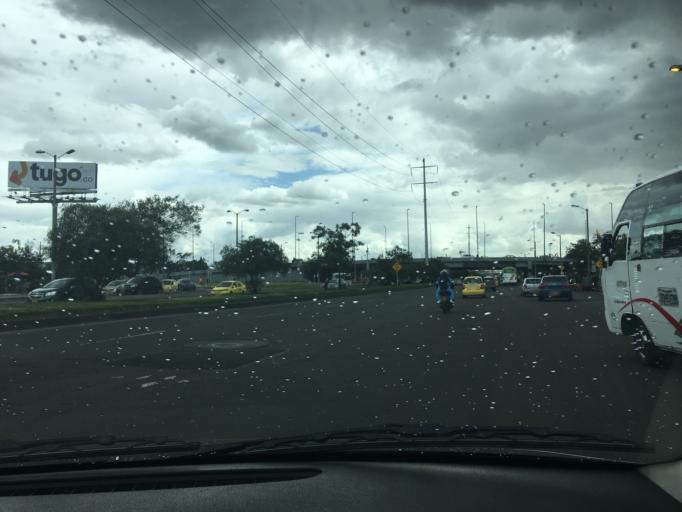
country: CO
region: Bogota D.C.
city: Barrio San Luis
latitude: 4.6850
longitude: -74.0779
